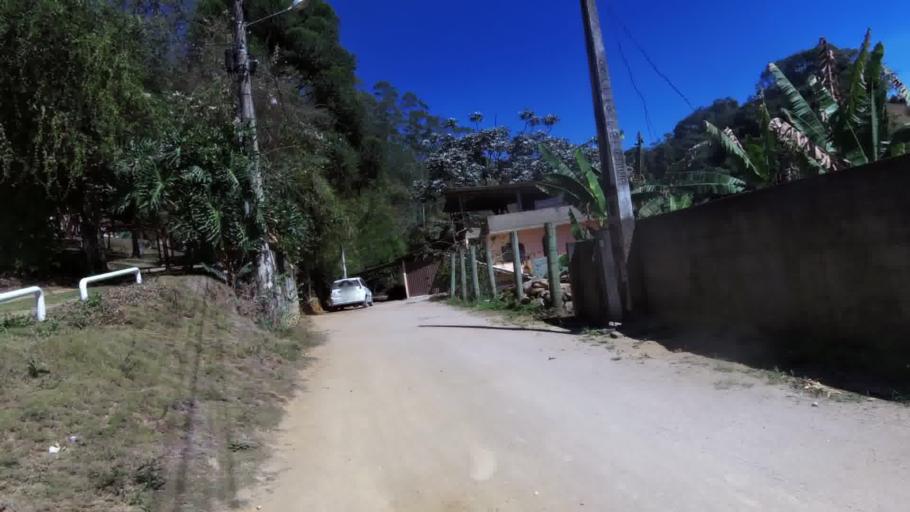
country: BR
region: Espirito Santo
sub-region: Vargem Alta
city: Vargem Alta
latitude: -20.6767
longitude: -41.0139
